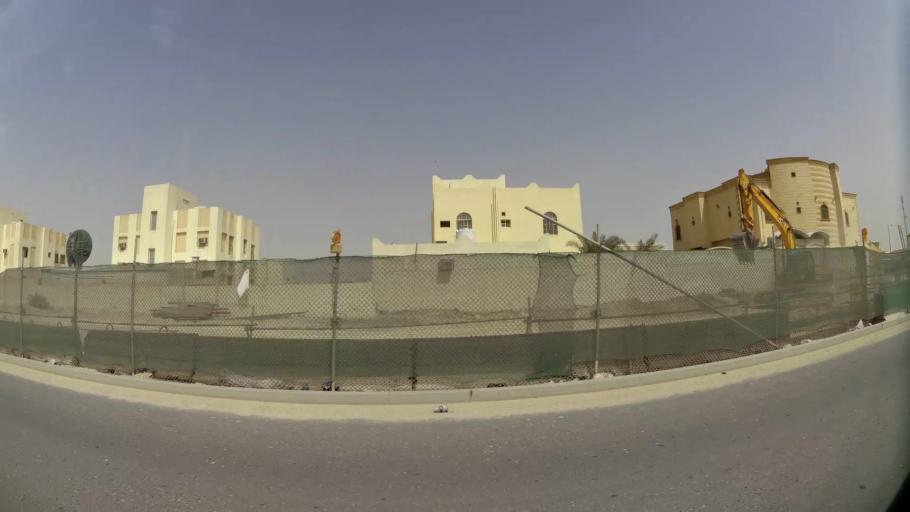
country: QA
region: Baladiyat ar Rayyan
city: Ar Rayyan
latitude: 25.2481
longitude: 51.3616
